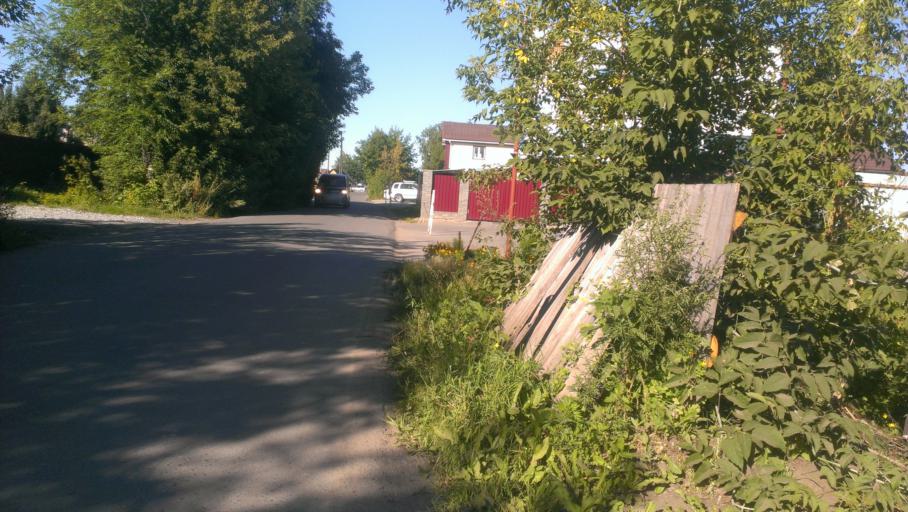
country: RU
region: Altai Krai
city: Novosilikatnyy
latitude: 53.3197
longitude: 83.6773
